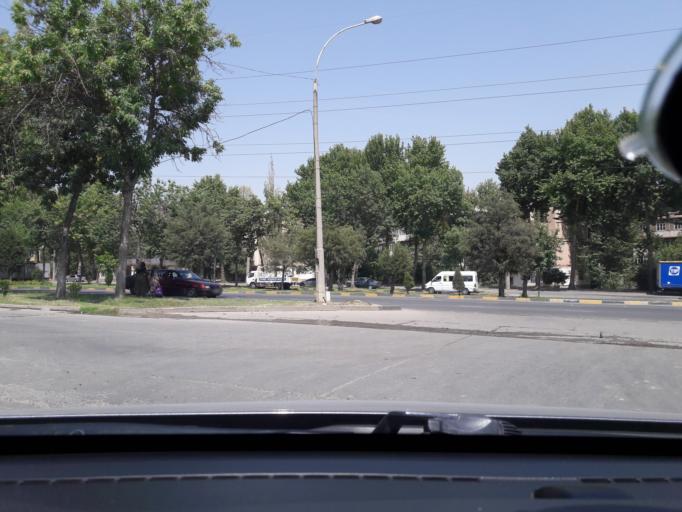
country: TJ
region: Dushanbe
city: Dushanbe
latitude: 38.5875
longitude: 68.7406
